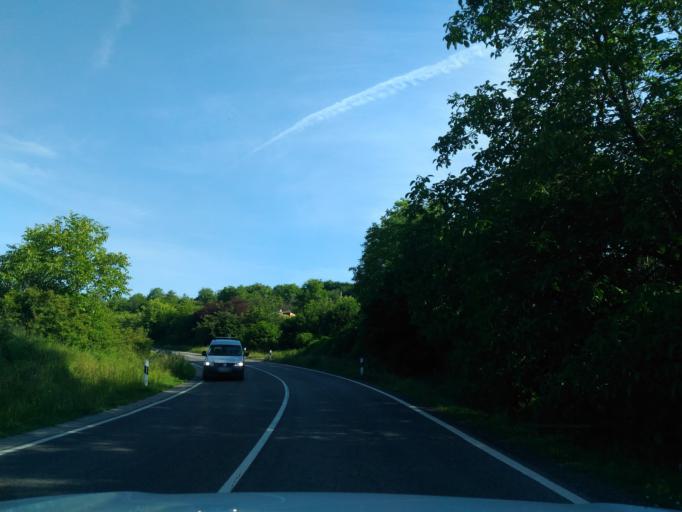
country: HU
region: Baranya
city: Komlo
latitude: 46.1727
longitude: 18.2630
